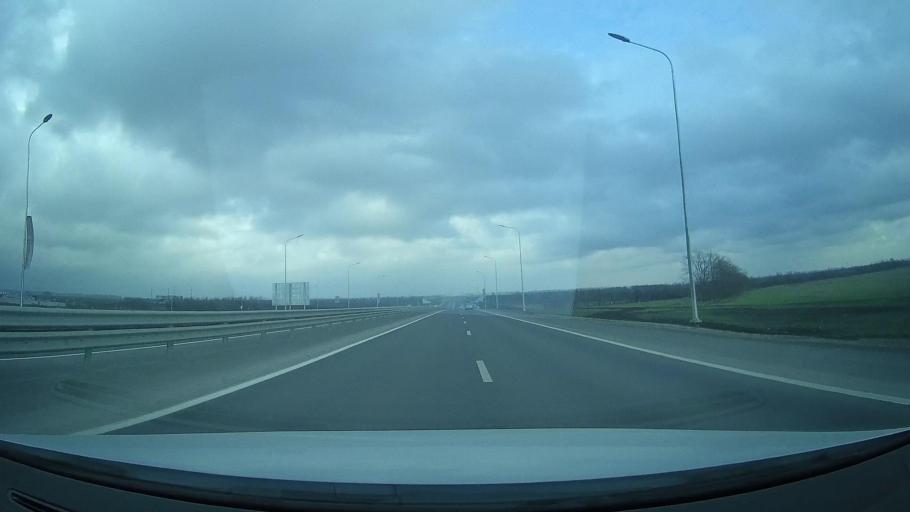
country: RU
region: Rostov
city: Grushevskaya
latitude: 47.4894
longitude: 39.9426
